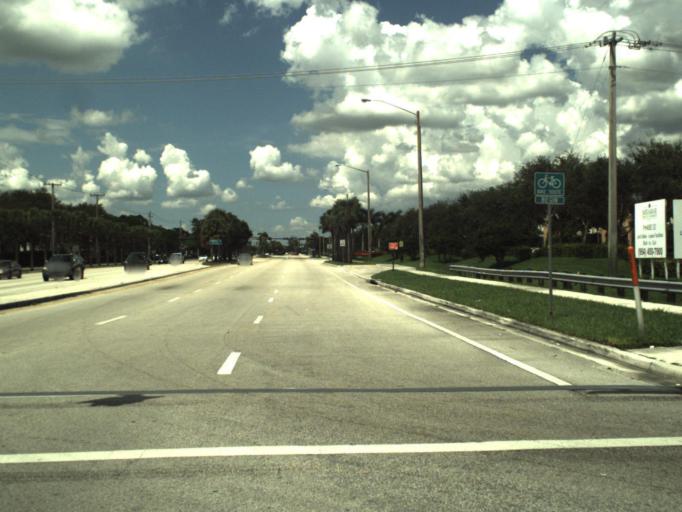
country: US
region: Florida
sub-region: Miami-Dade County
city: Lake Lucerne
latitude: 25.9807
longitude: -80.2789
